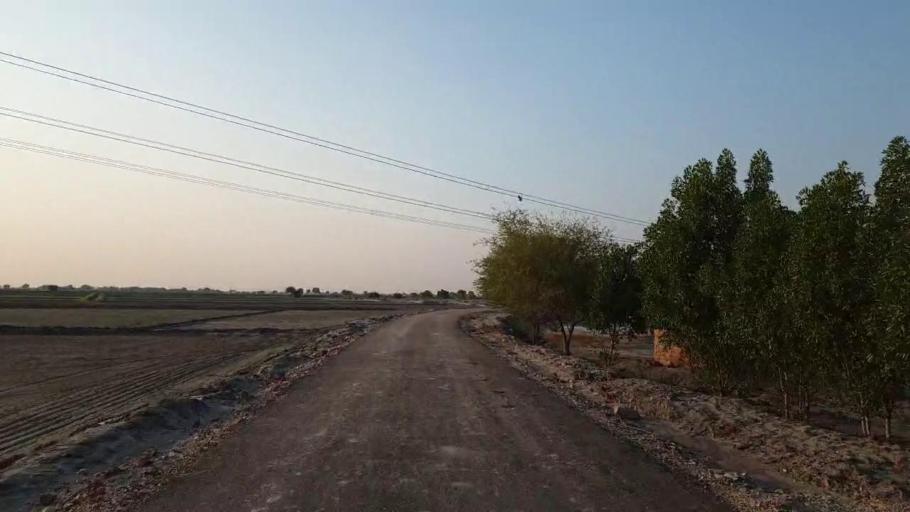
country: PK
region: Sindh
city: Sehwan
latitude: 26.4322
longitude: 67.7649
